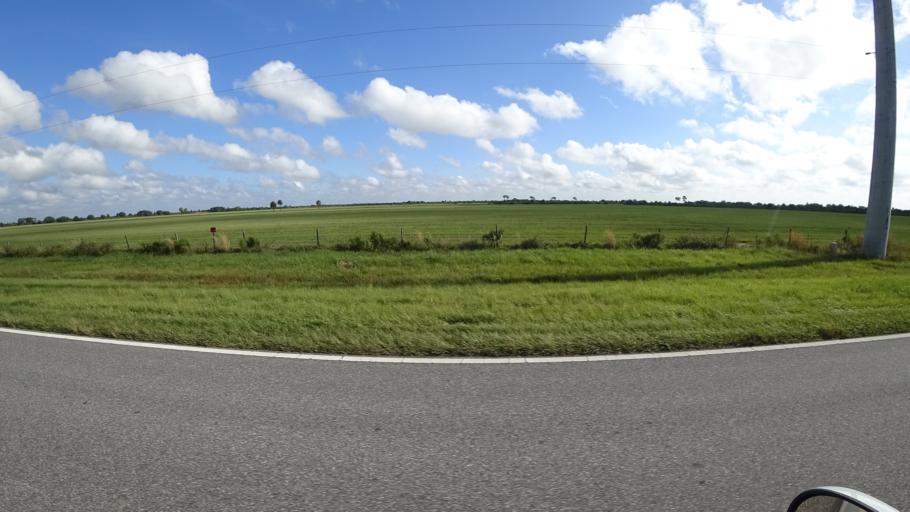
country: US
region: Florida
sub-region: Hillsborough County
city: Wimauma
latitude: 27.5228
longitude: -82.3308
